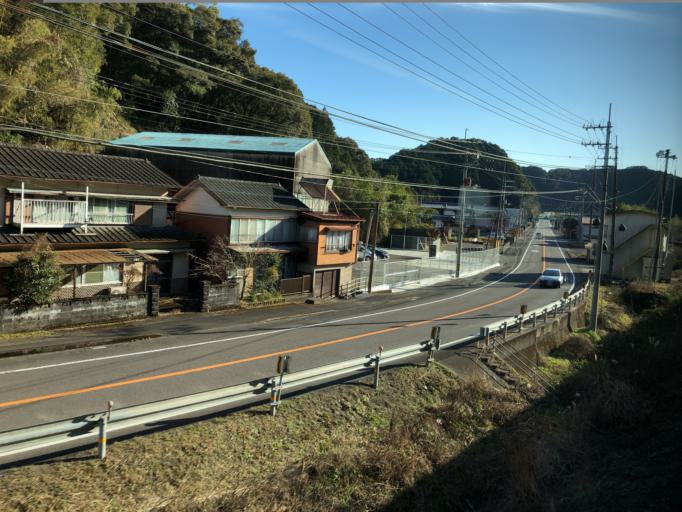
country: JP
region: Kochi
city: Nakamura
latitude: 33.1081
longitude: 133.0990
